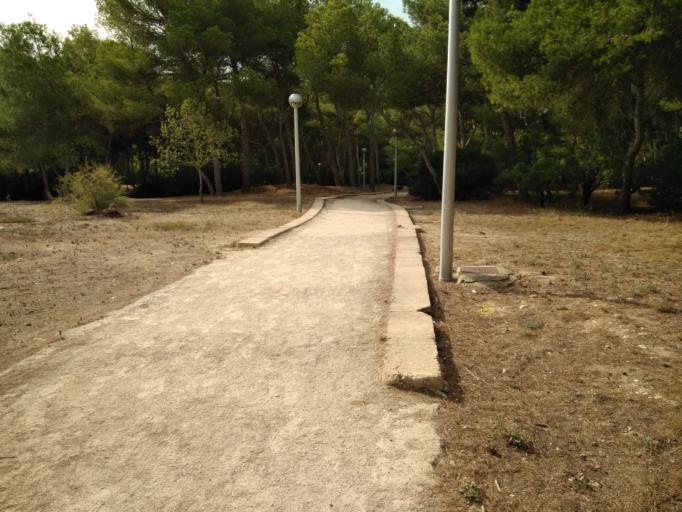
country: ES
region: Balearic Islands
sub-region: Illes Balears
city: s'Arenal
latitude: 39.5290
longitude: 2.7377
